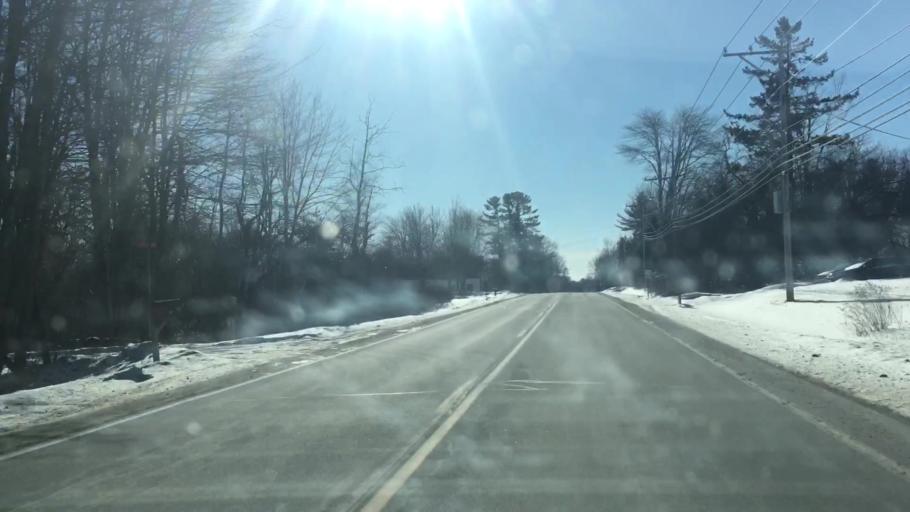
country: US
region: Maine
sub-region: Hancock County
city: Ellsworth
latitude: 44.5062
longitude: -68.4398
